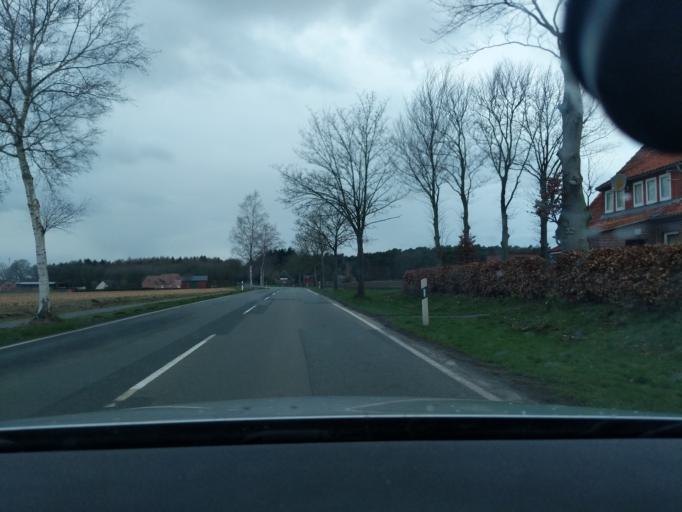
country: DE
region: Lower Saxony
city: Kutenholz
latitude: 53.4915
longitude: 9.3030
